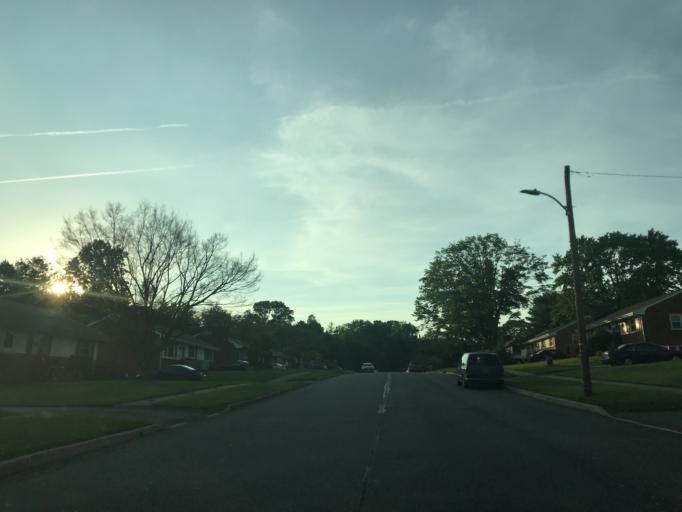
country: US
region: Maryland
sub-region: Harford County
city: North Bel Air
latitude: 39.5318
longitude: -76.3557
